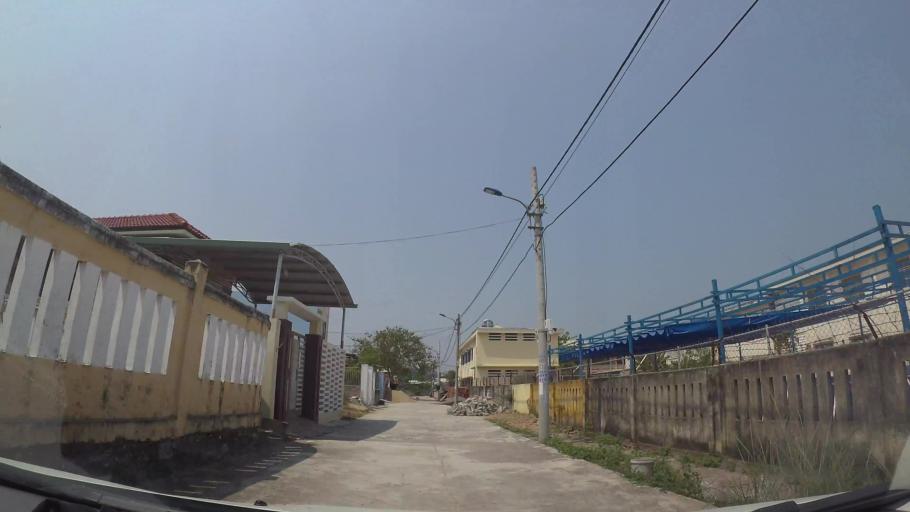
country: VN
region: Da Nang
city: Ngu Hanh Son
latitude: 15.9940
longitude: 108.2632
